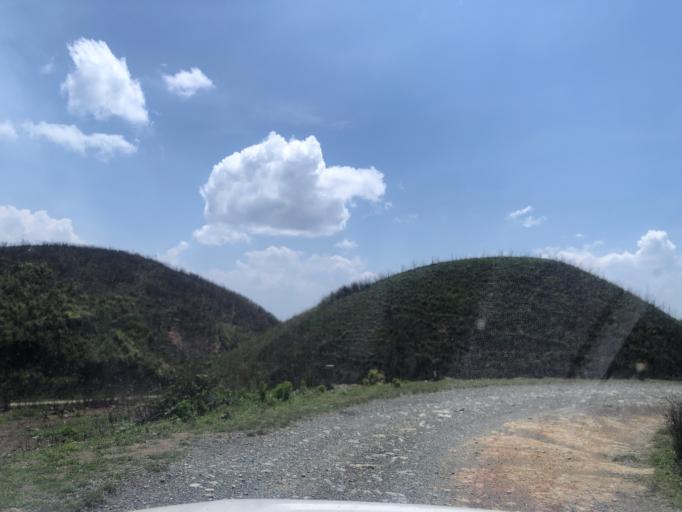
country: LA
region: Phongsali
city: Phongsali
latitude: 21.4112
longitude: 102.1873
